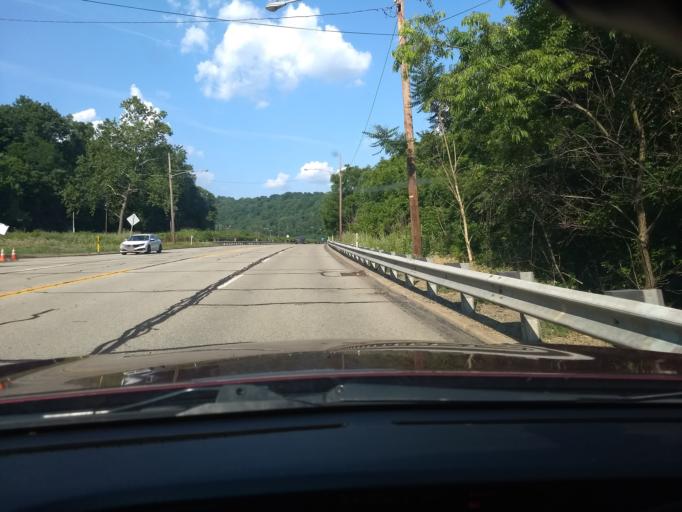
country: US
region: Pennsylvania
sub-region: Allegheny County
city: Versailles
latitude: 40.3221
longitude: -79.8257
